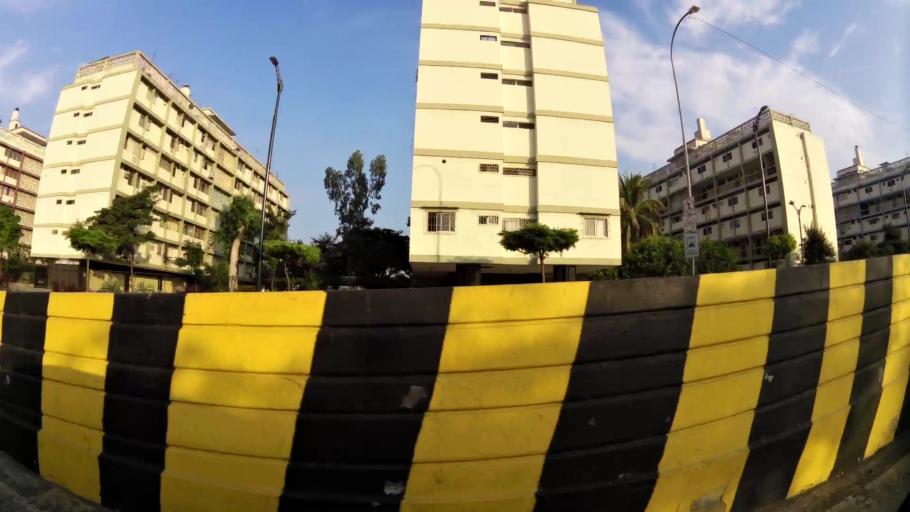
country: EC
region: Guayas
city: Guayaquil
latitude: -2.2093
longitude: -79.8953
